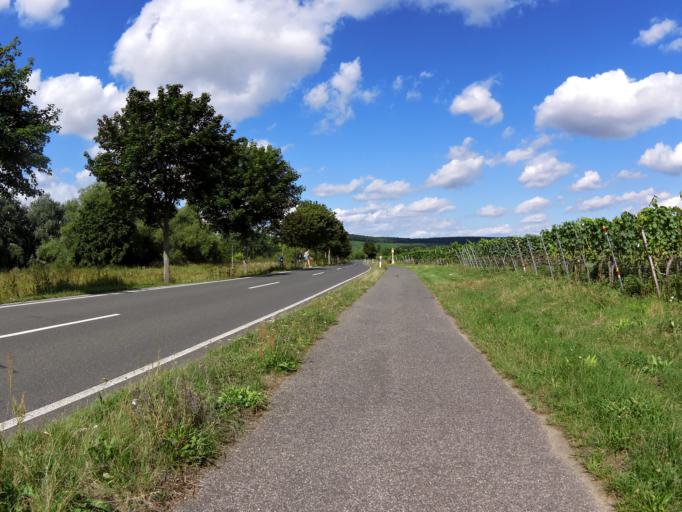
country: DE
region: Bavaria
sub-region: Regierungsbezirk Unterfranken
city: Sommerach
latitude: 49.8323
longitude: 10.1920
